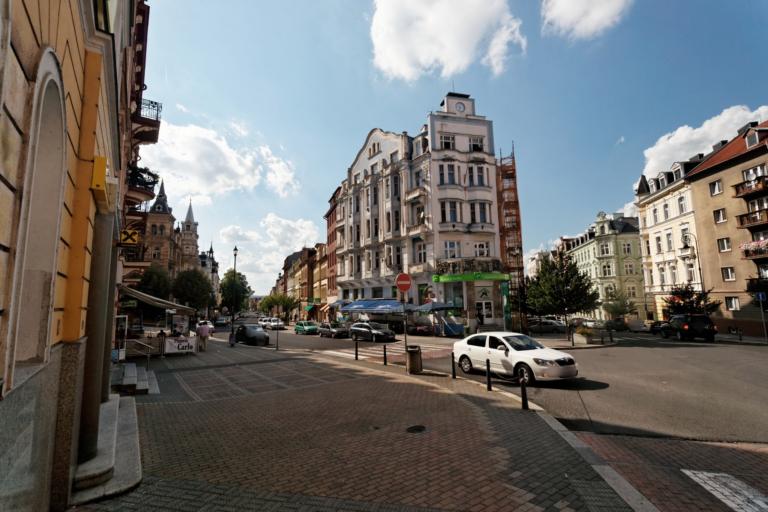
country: CZ
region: Karlovarsky
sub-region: Okres Karlovy Vary
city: Karlovy Vary
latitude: 50.2290
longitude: 12.8698
